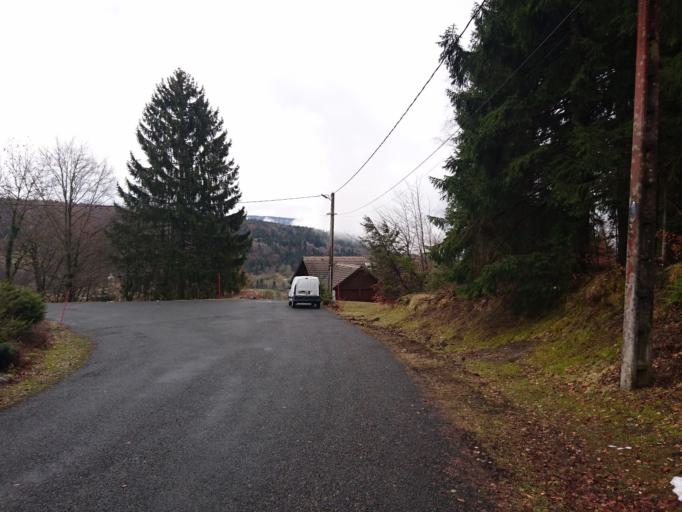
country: FR
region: Rhone-Alpes
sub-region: Departement de l'Ain
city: Nantua
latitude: 46.1862
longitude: 5.6758
